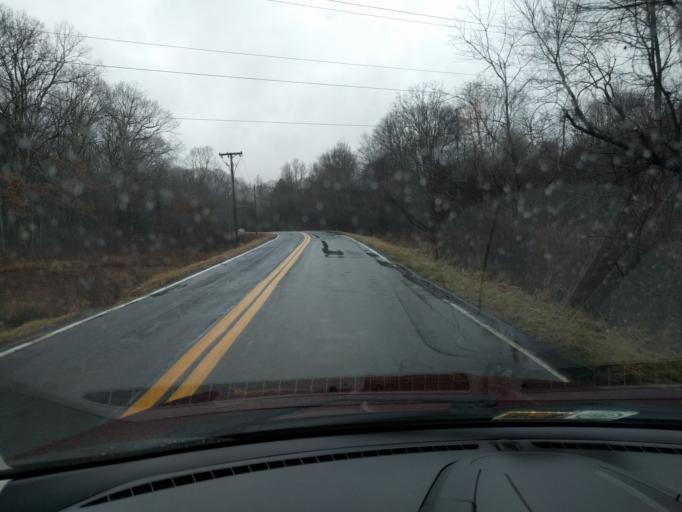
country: US
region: West Virginia
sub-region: Raleigh County
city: Beckley
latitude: 37.7949
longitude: -81.1970
